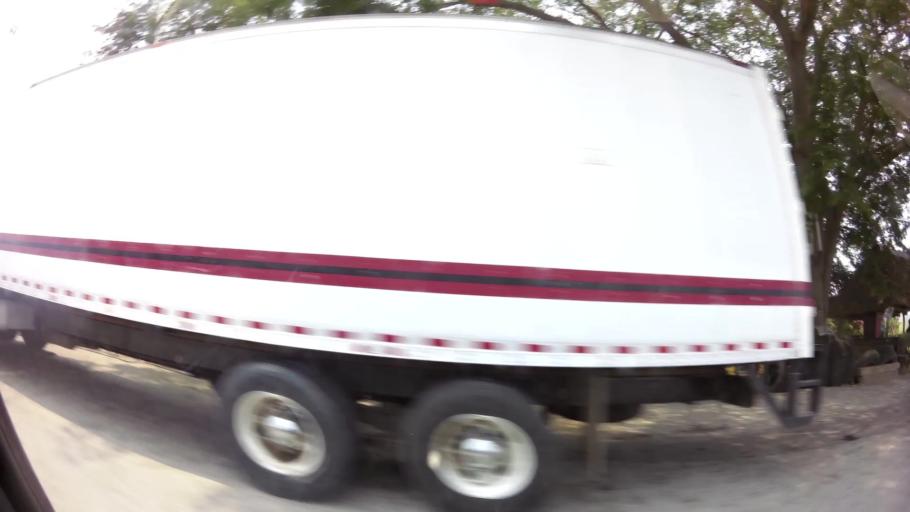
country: HN
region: Yoro
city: El Progreso
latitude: 15.4118
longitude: -87.8517
